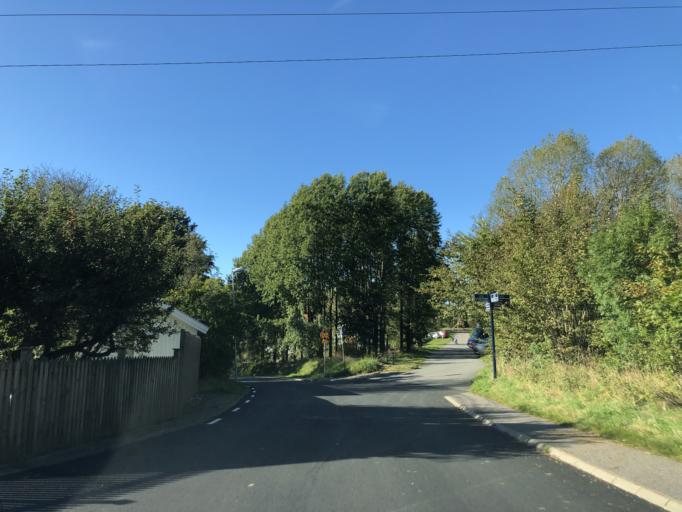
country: SE
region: Vaestra Goetaland
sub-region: Molndal
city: Moelndal
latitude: 57.6821
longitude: 12.0230
